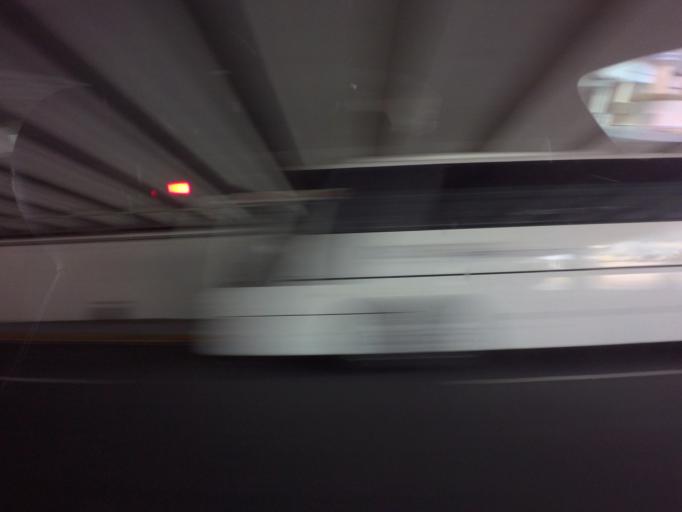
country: PH
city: Sambayanihan People's Village
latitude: 14.5143
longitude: 120.9784
